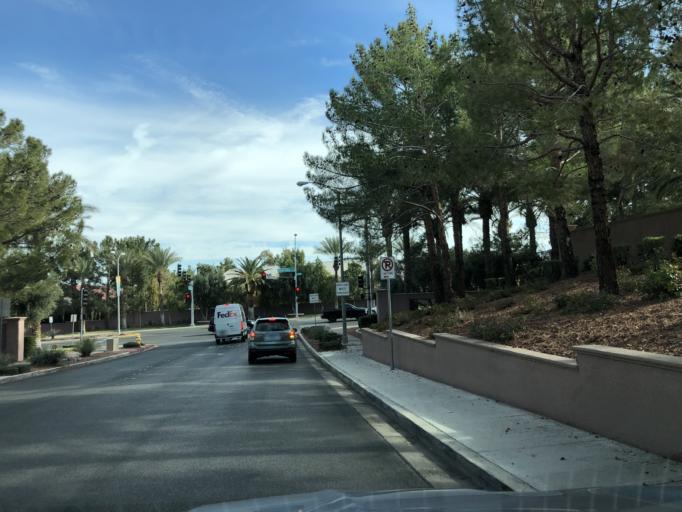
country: US
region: Nevada
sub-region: Clark County
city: Whitney
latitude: 36.0147
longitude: -115.0838
